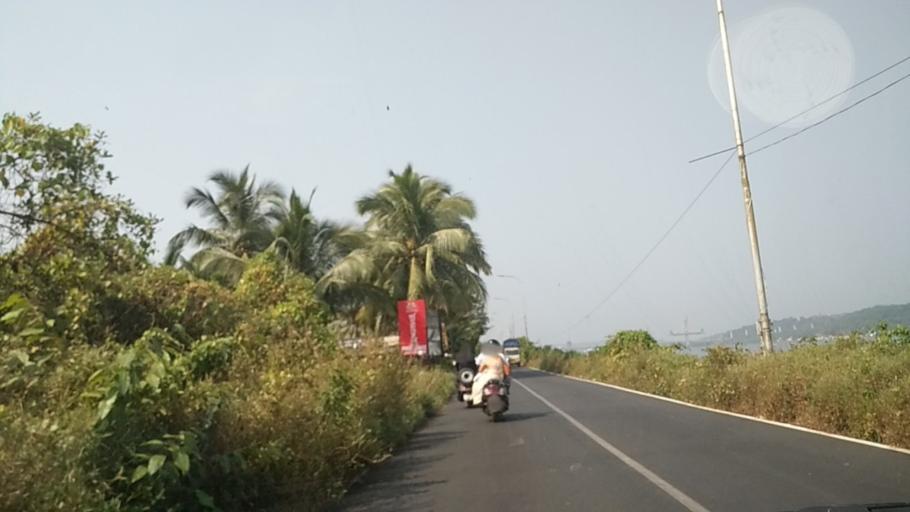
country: IN
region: Goa
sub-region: North Goa
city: Panaji
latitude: 15.5026
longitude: 73.8548
